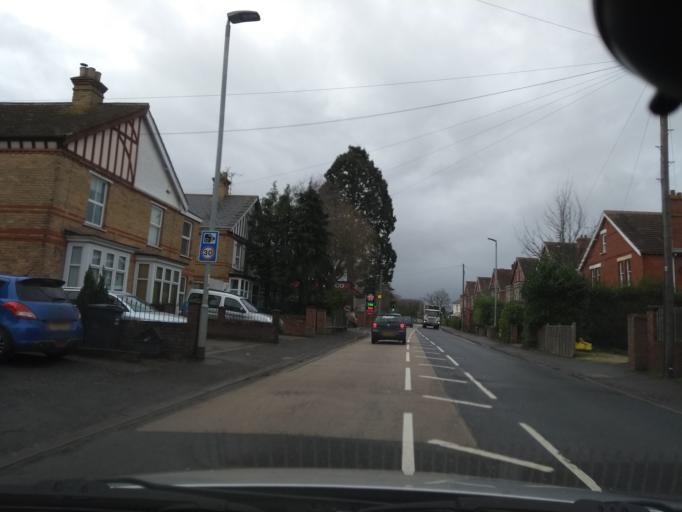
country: GB
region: England
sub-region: Somerset
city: Taunton
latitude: 51.0284
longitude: -3.1154
